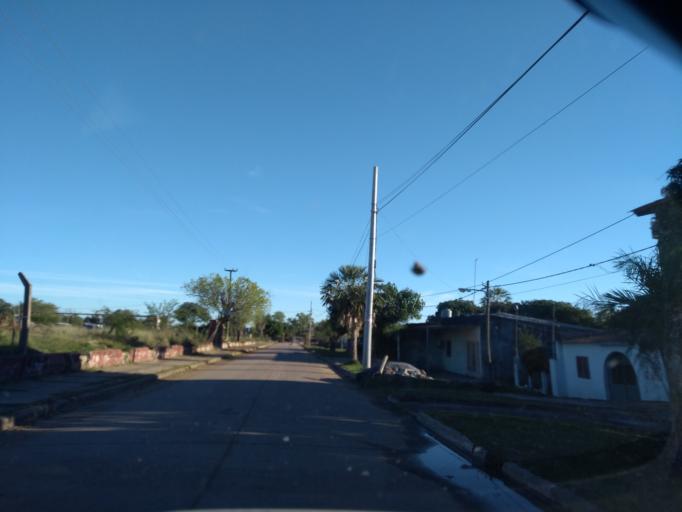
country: AR
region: Chaco
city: Puerto Vilelas
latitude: -27.4997
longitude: -58.9331
